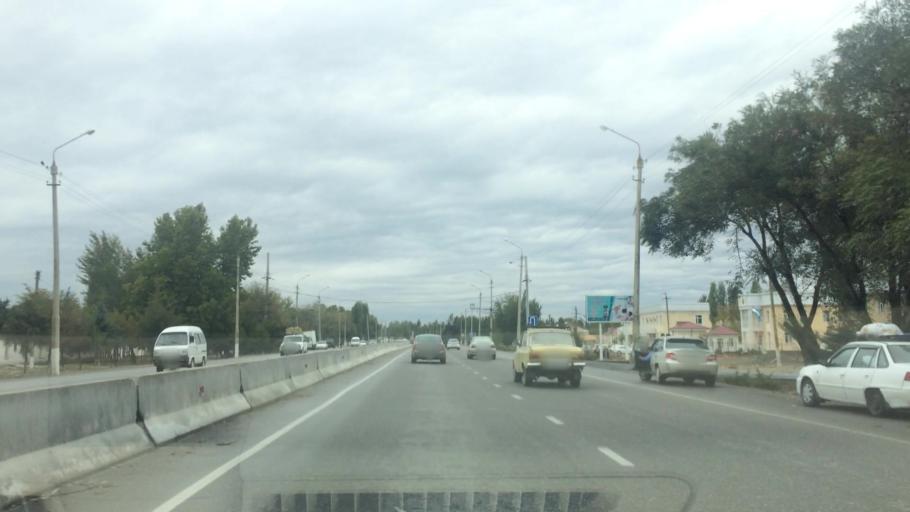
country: UZ
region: Jizzax
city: Jizzax
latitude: 39.9994
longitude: 67.5901
